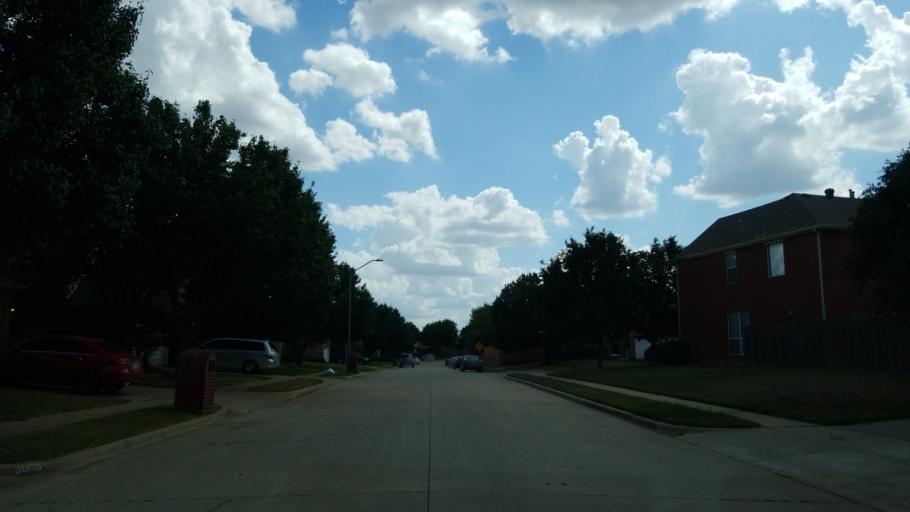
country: US
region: Texas
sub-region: Tarrant County
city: Euless
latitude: 32.8793
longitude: -97.0788
